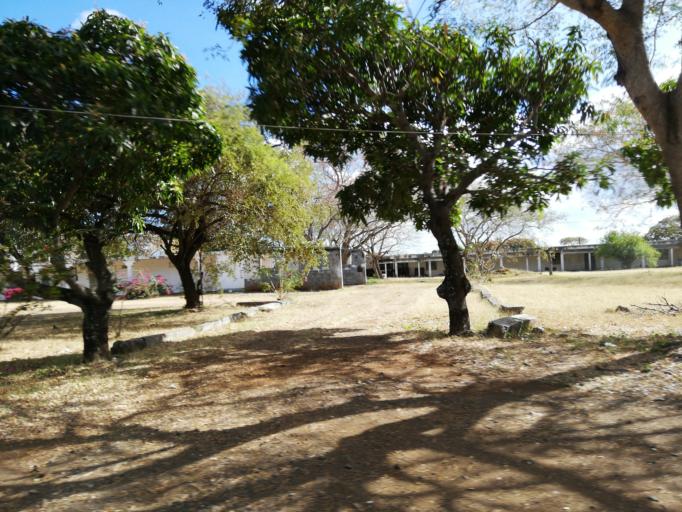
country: MU
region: Moka
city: Pailles
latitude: -20.1871
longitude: 57.4709
